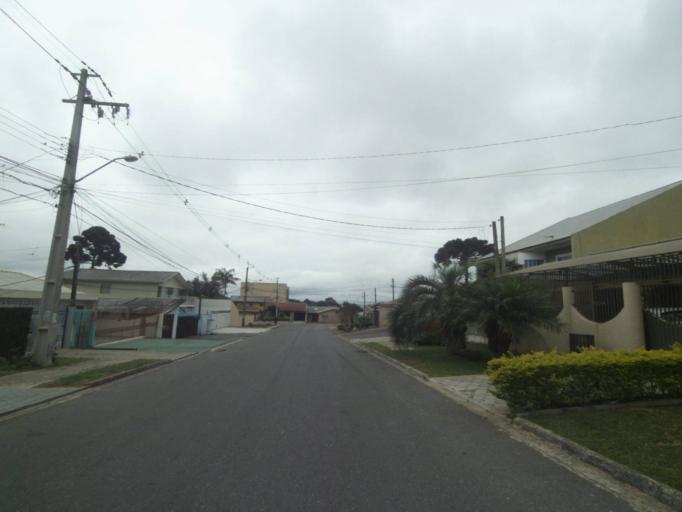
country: BR
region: Parana
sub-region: Sao Jose Dos Pinhais
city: Sao Jose dos Pinhais
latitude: -25.5457
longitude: -49.2815
